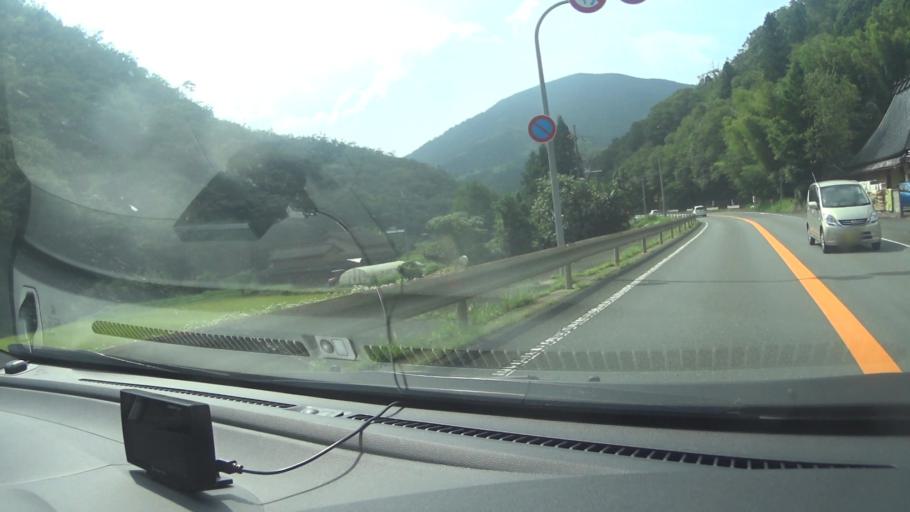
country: JP
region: Hyogo
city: Sasayama
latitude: 35.1488
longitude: 135.3545
